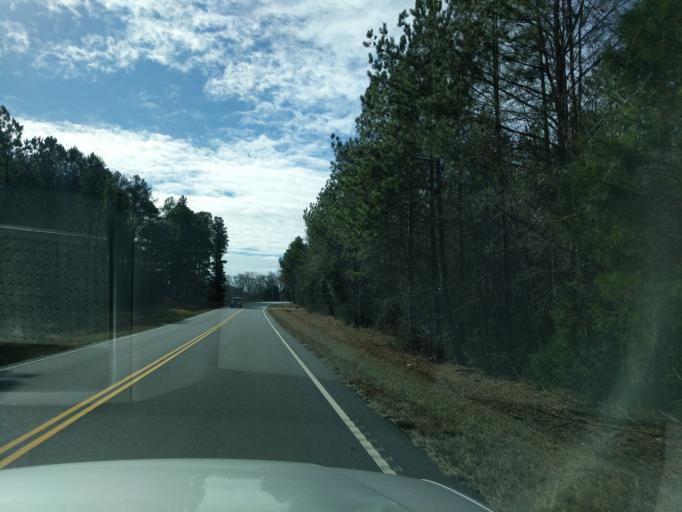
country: US
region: South Carolina
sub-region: Saluda County
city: Saluda
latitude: 33.9567
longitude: -81.9011
